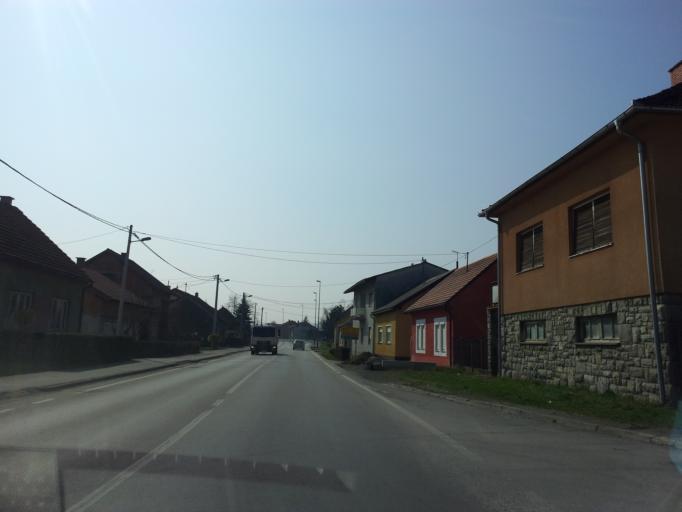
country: HR
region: Karlovacka
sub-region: Grad Karlovac
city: Karlovac
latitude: 45.4697
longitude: 15.5588
